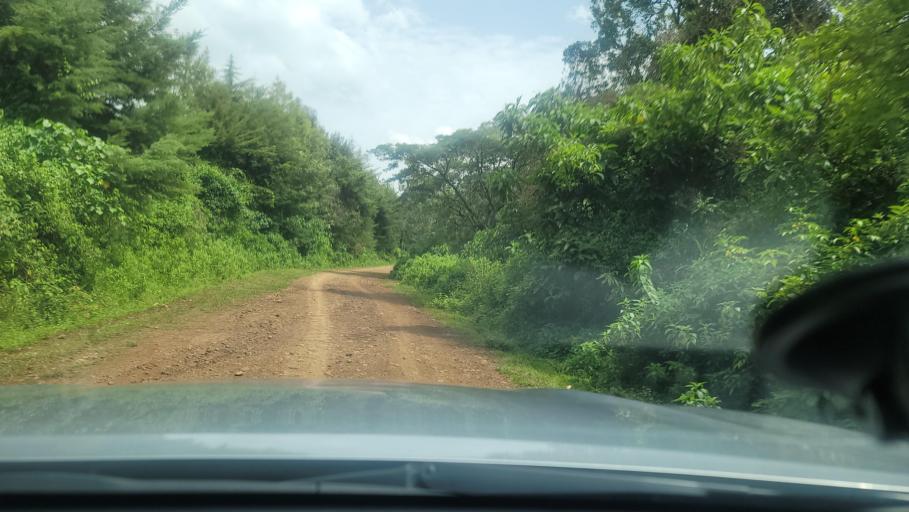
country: ET
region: Oromiya
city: Agaro
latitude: 7.8056
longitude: 36.4151
